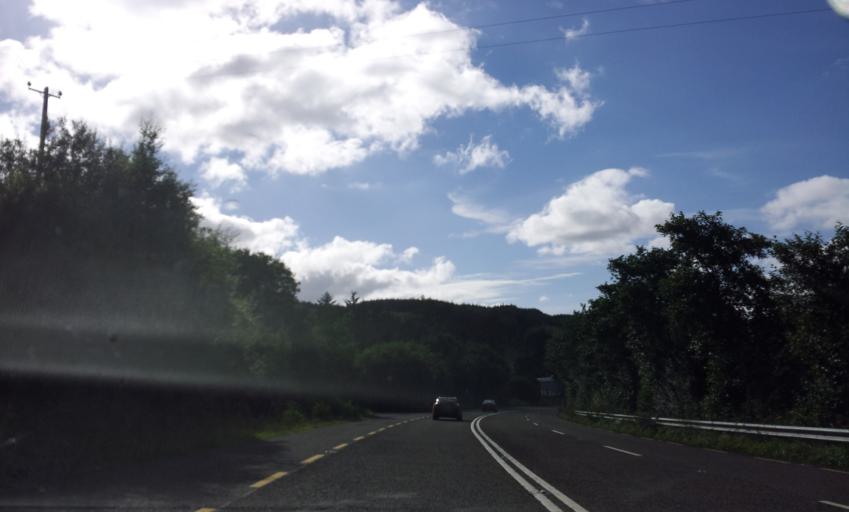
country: IE
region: Munster
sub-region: County Cork
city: Millstreet
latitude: 51.9820
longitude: -9.2740
